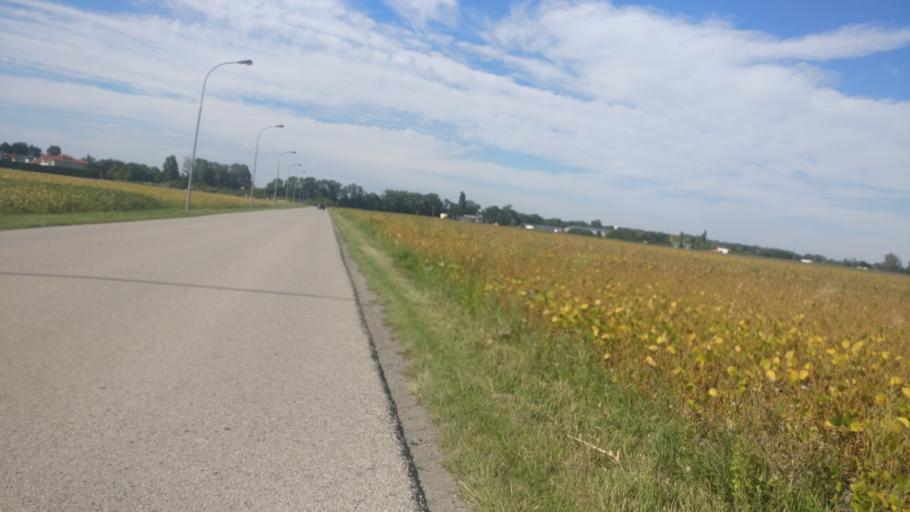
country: AT
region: Lower Austria
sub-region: Politischer Bezirk Baden
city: Ebreichsdorf
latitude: 47.9670
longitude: 16.4145
